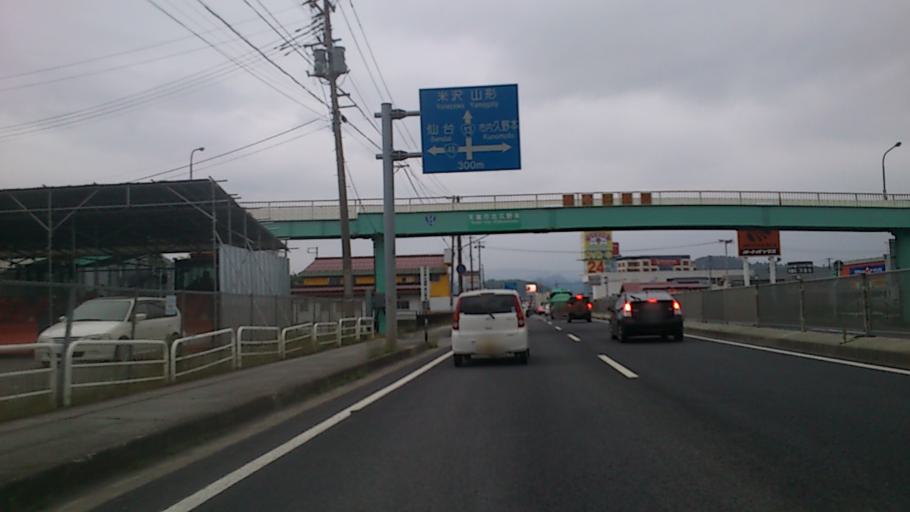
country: JP
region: Yamagata
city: Tendo
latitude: 38.3775
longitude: 140.3826
